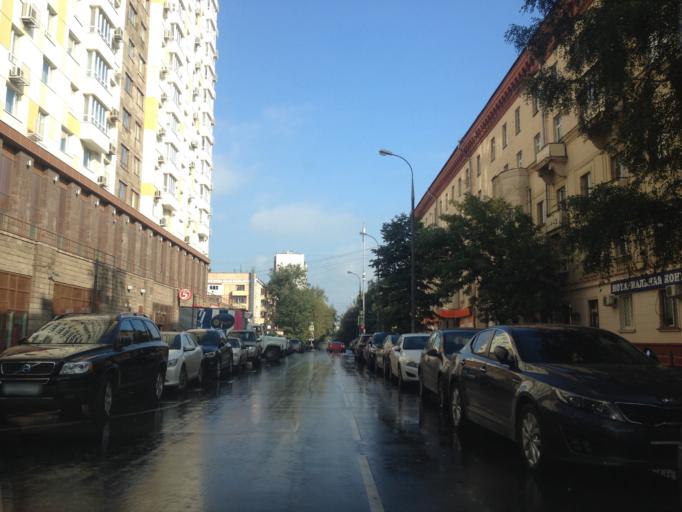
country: RU
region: Moskovskaya
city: Izmaylovo
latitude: 55.7920
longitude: 37.7883
